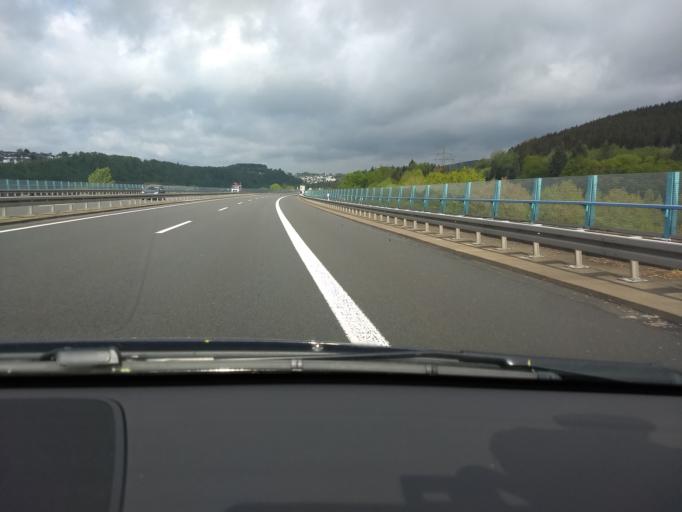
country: DE
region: North Rhine-Westphalia
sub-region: Regierungsbezirk Arnsberg
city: Arnsberg
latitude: 51.3939
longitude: 8.1019
